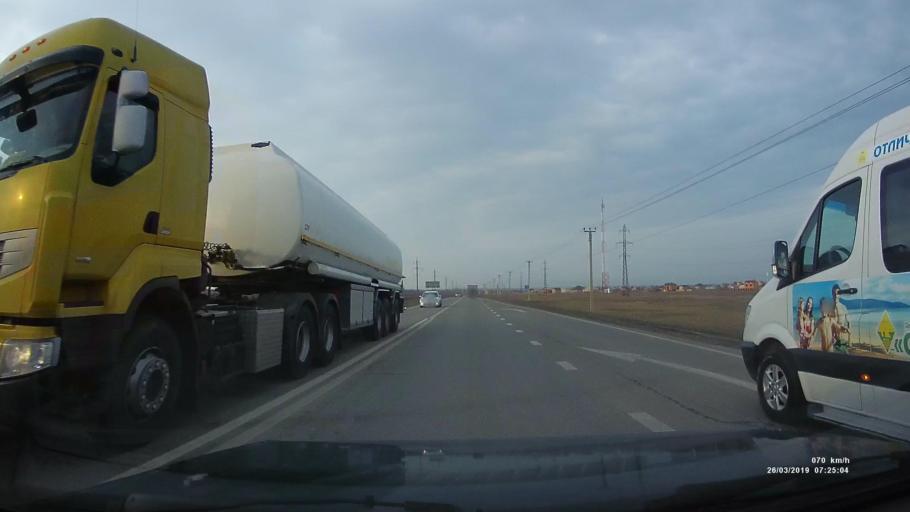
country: RU
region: Rostov
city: Taganrog
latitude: 47.2739
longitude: 38.8534
